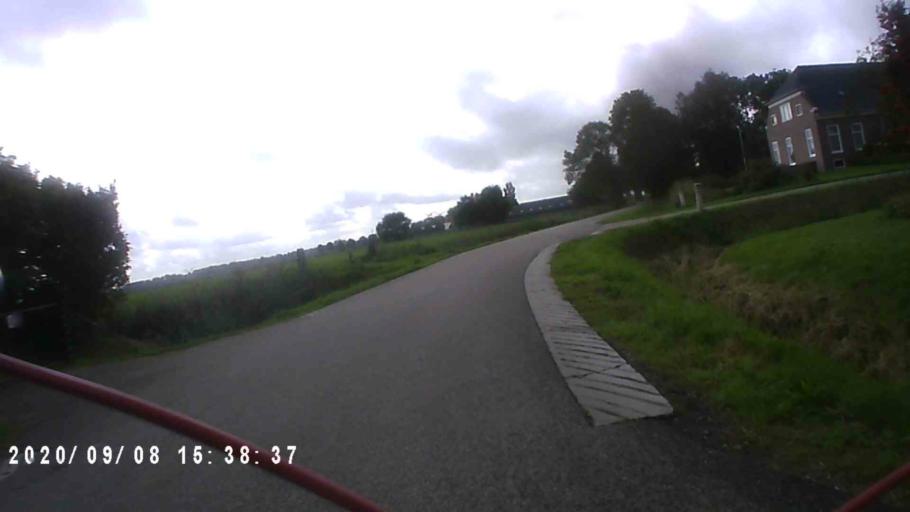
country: NL
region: Groningen
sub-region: Gemeente Bedum
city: Bedum
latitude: 53.2794
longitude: 6.6125
